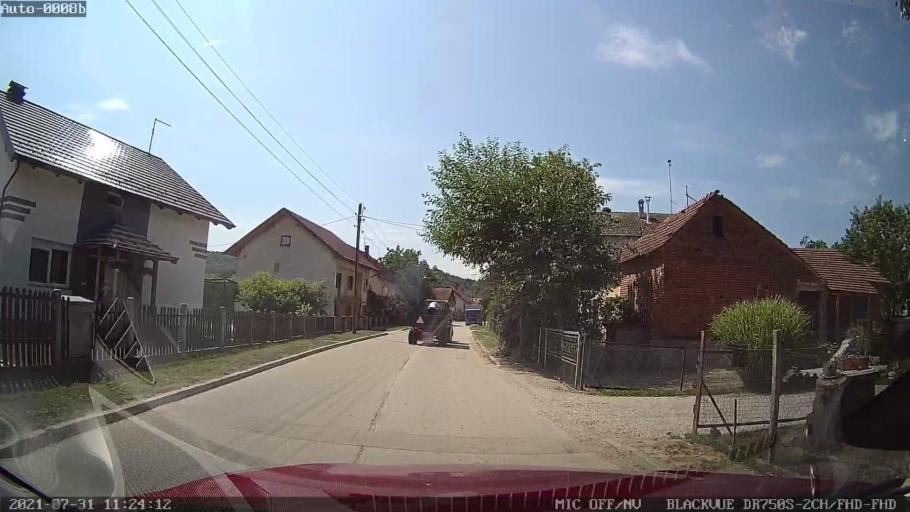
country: HR
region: Varazdinska
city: Jalzabet
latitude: 46.2115
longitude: 16.4582
